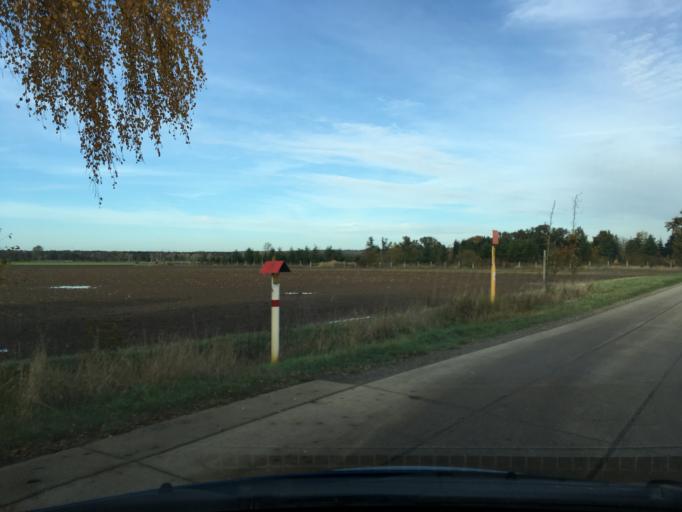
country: DE
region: Lower Saxony
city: Artlenburg
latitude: 53.3628
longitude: 10.4698
